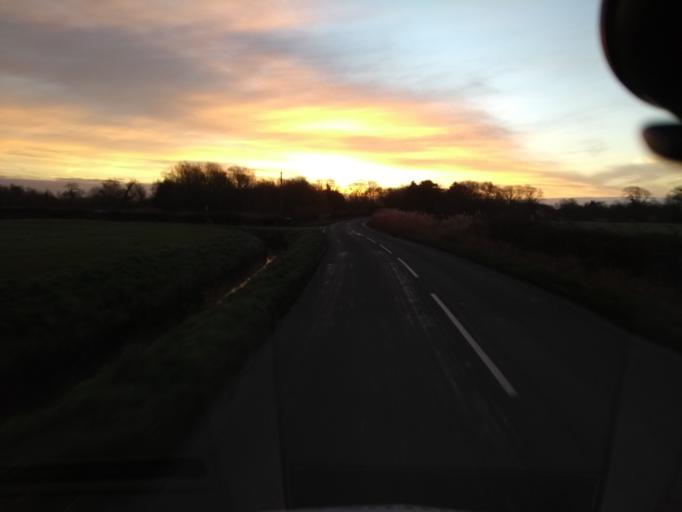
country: GB
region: England
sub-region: Somerset
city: Highbridge
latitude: 51.2247
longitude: -2.9403
